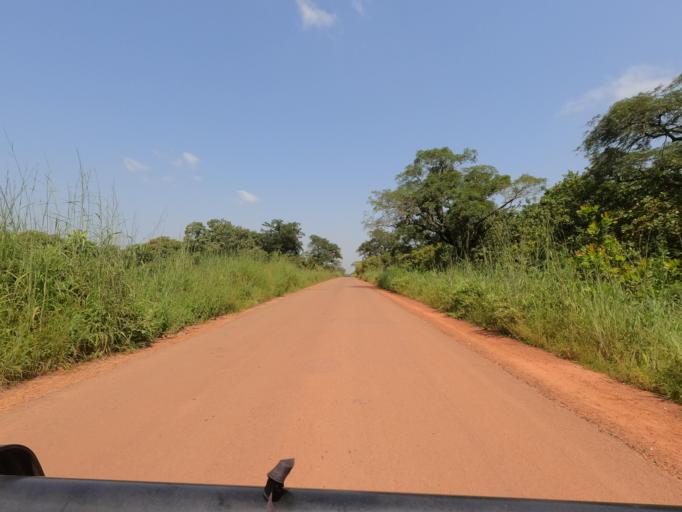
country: GW
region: Oio
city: Bissora
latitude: 12.3397
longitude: -15.7619
